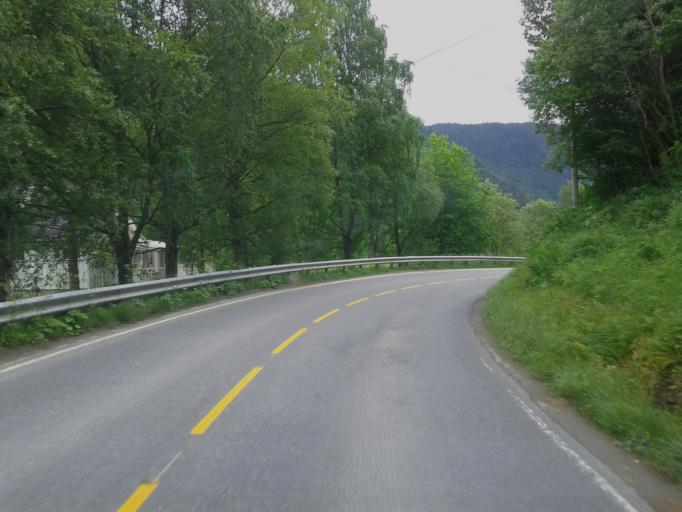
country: NO
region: Sor-Trondelag
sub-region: Midtre Gauldal
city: Storen
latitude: 62.9933
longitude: 10.5005
